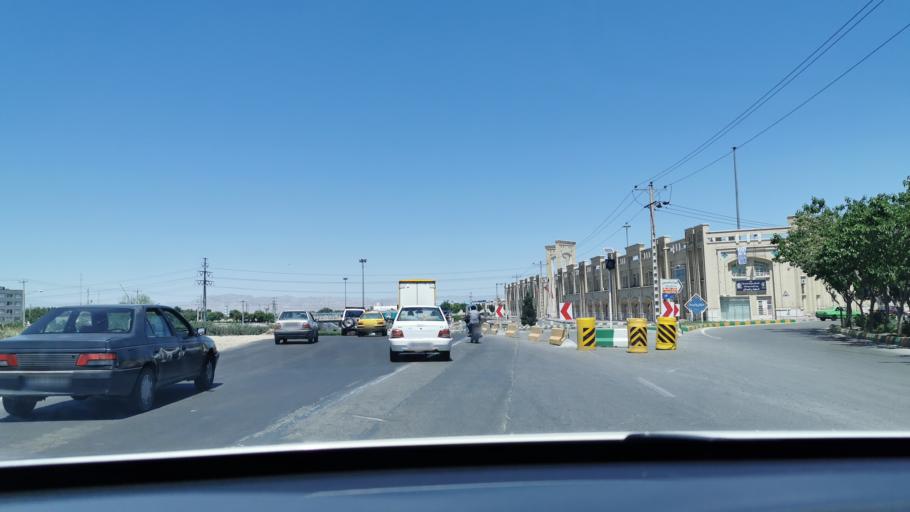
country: IR
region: Razavi Khorasan
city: Mashhad
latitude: 36.2607
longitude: 59.6487
